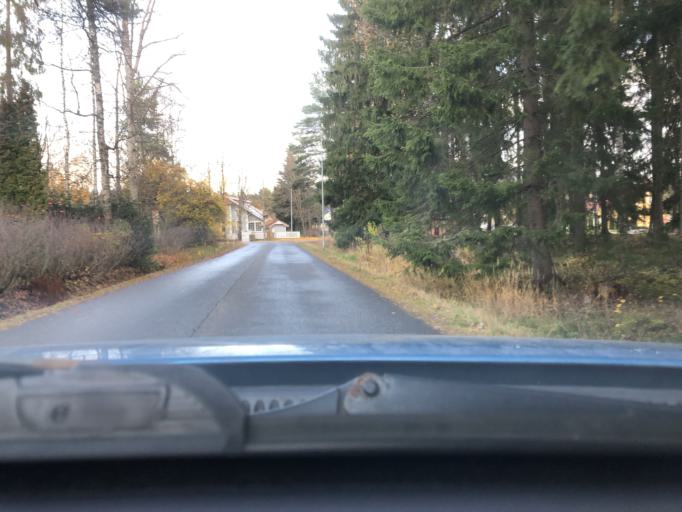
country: FI
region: Pirkanmaa
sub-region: Tampere
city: Kangasala
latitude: 61.4685
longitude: 24.0292
